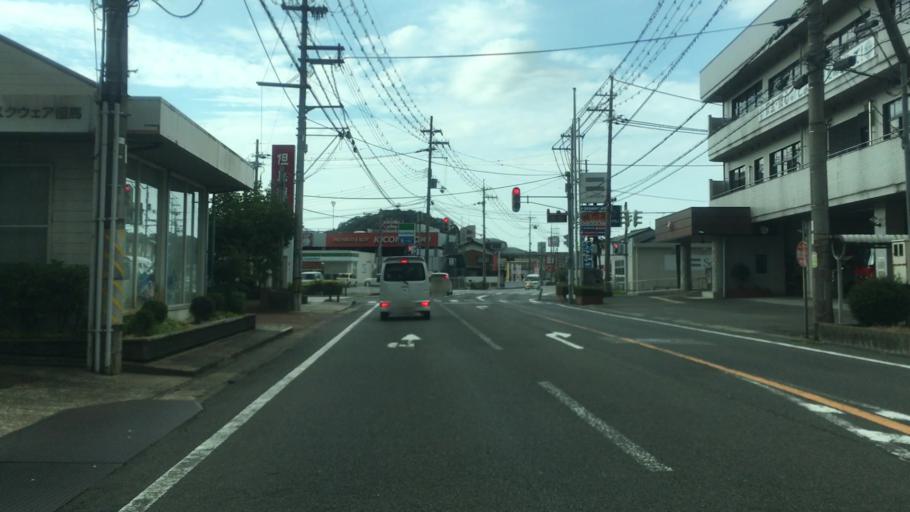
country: JP
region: Hyogo
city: Toyooka
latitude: 35.5307
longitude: 134.8198
